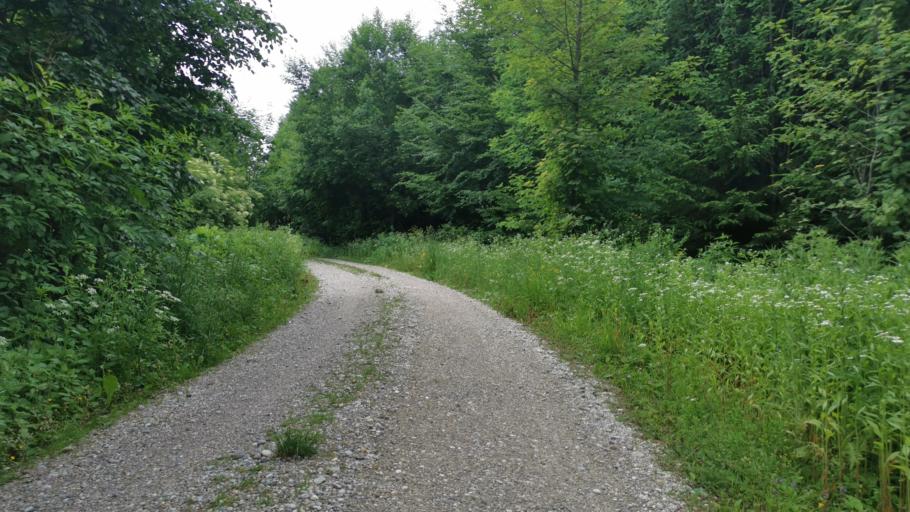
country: DE
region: Bavaria
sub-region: Upper Bavaria
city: Schaftlarn
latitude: 48.0085
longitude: 11.4666
